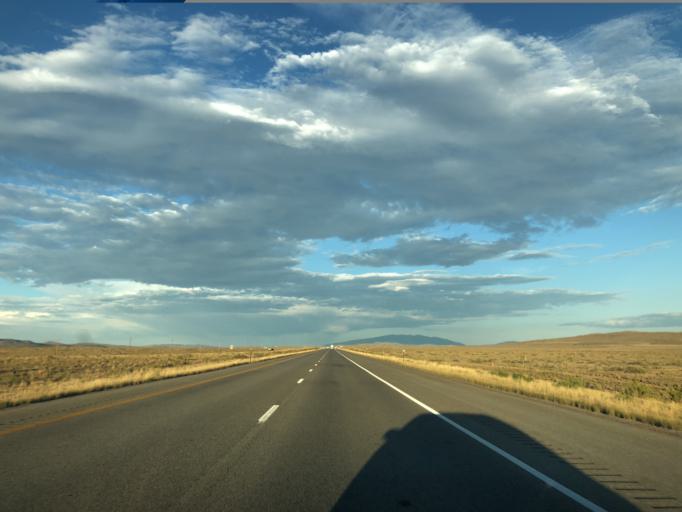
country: US
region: Wyoming
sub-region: Carbon County
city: Rawlins
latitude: 41.7643
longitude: -107.0198
